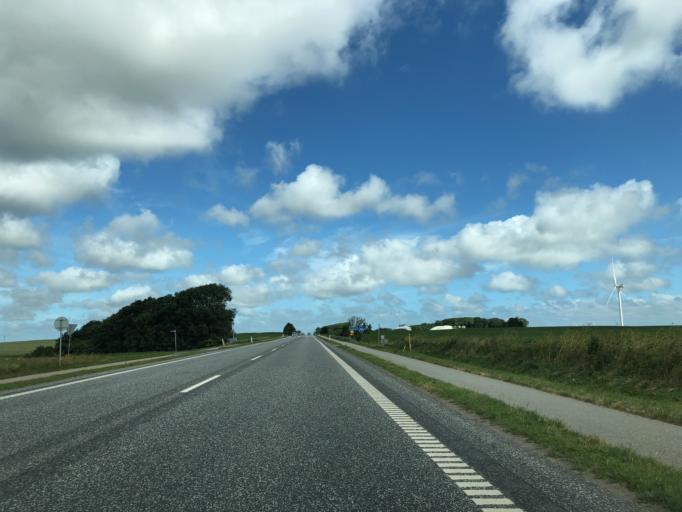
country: DK
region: Central Jutland
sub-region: Holstebro Kommune
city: Holstebro
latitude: 56.4199
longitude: 8.6014
